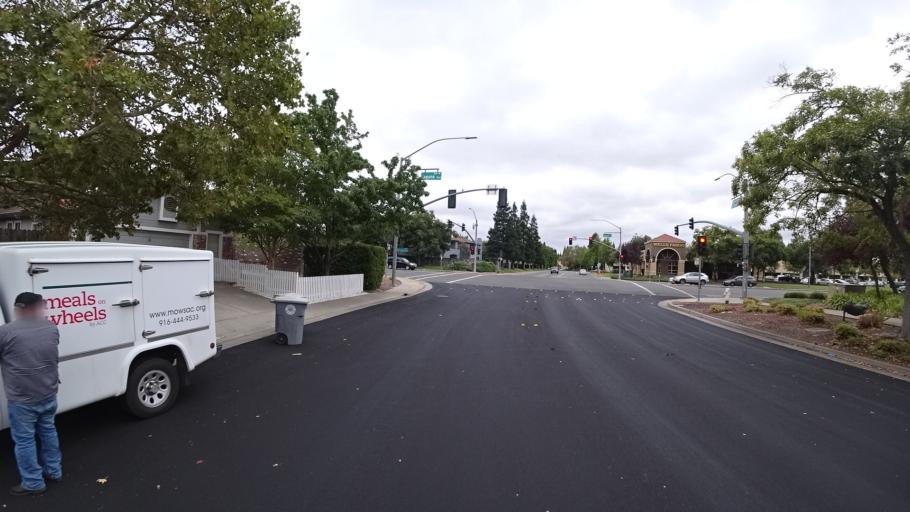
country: US
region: California
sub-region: Sacramento County
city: Laguna
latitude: 38.4237
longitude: -121.4446
